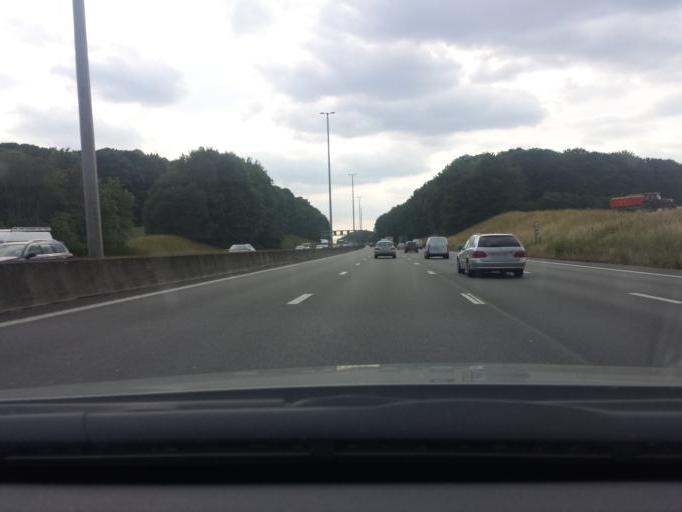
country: BE
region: Flanders
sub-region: Provincie Vlaams-Brabant
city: Kortenberg
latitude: 50.8687
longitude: 4.5603
